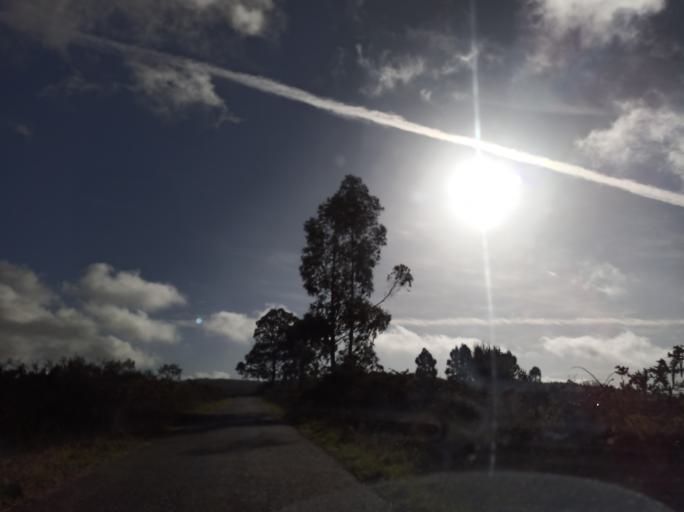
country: ES
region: Galicia
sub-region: Provincia da Coruna
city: Sobrado
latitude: 43.0802
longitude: -7.9567
